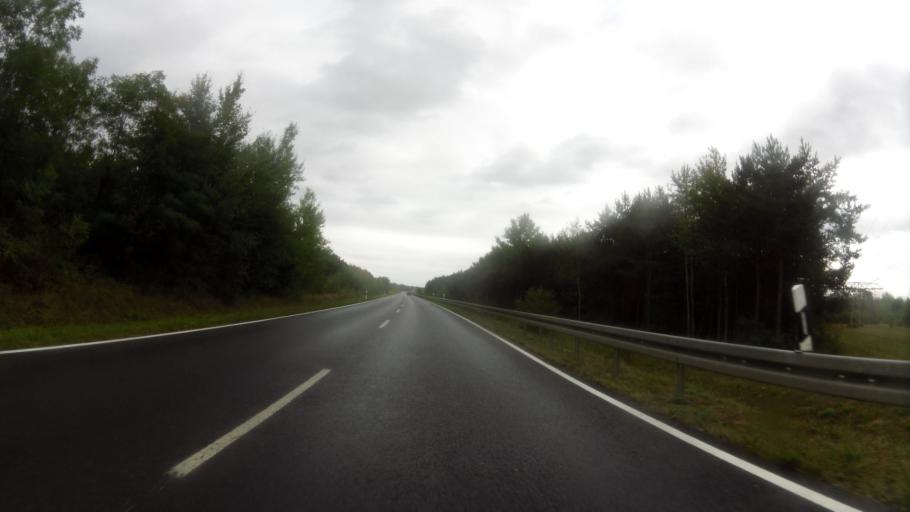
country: DE
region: Brandenburg
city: Spremberg
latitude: 51.5646
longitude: 14.3295
